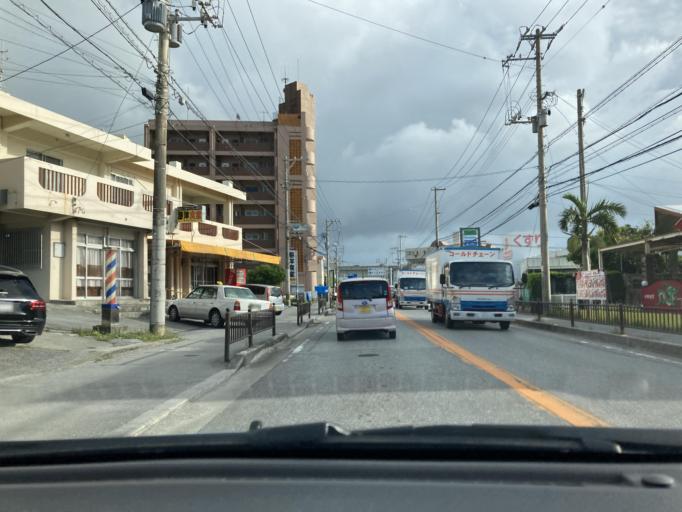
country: JP
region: Okinawa
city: Tomigusuku
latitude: 26.1770
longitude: 127.6654
